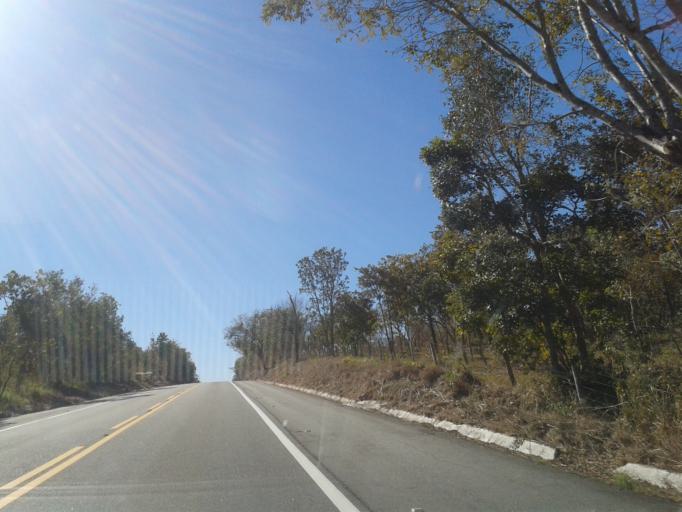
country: BR
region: Goias
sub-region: Goias
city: Goias
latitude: -15.7286
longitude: -50.1857
